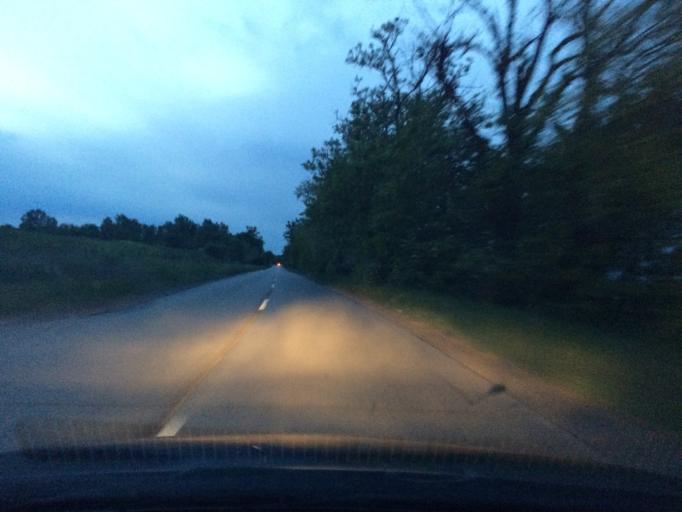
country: HU
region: Szabolcs-Szatmar-Bereg
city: Tiszavasvari
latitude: 47.9354
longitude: 21.3831
